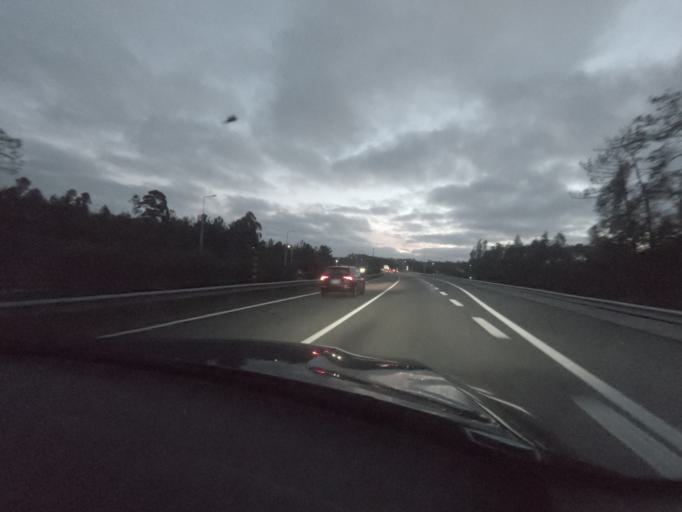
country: PT
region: Leiria
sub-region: Pombal
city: Pombal
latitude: 39.9415
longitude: -8.6777
